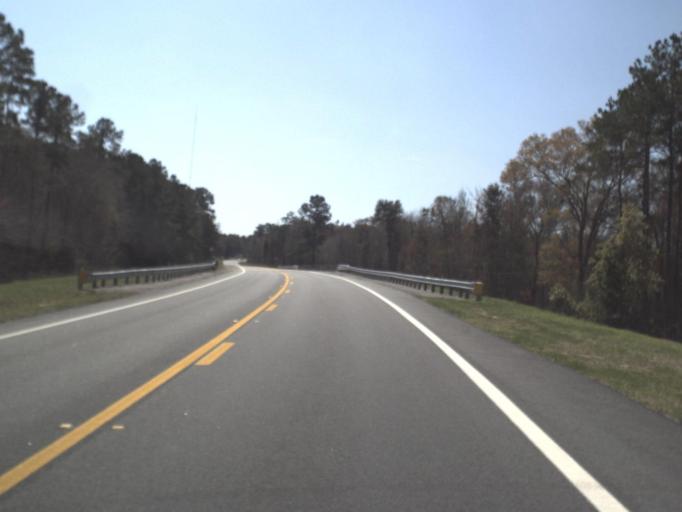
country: US
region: Florida
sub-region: Jefferson County
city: Monticello
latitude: 30.4760
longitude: -84.0225
